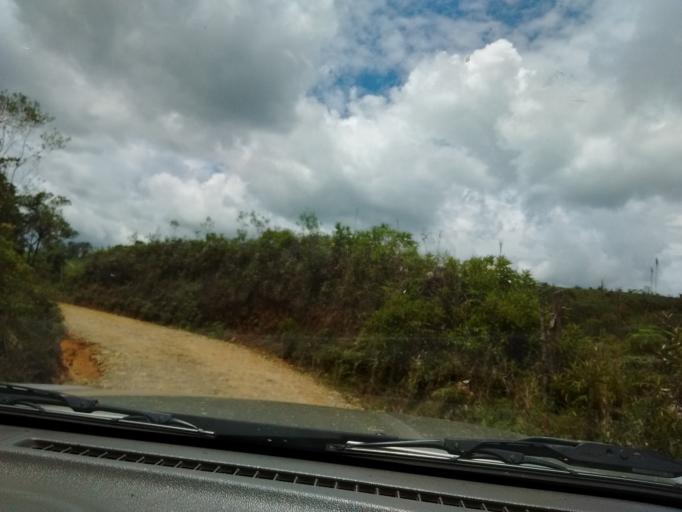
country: CO
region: Cauca
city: Villa Rica
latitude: 2.6060
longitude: -76.7506
